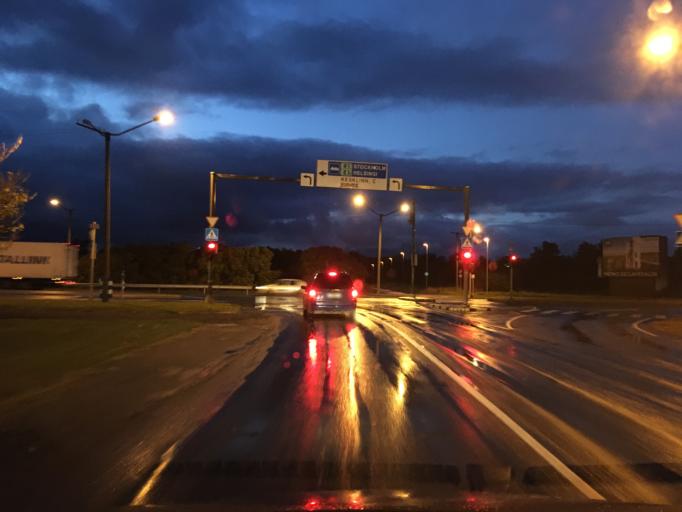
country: EE
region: Harju
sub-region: Viimsi vald
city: Viimsi
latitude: 59.4460
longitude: 24.8196
